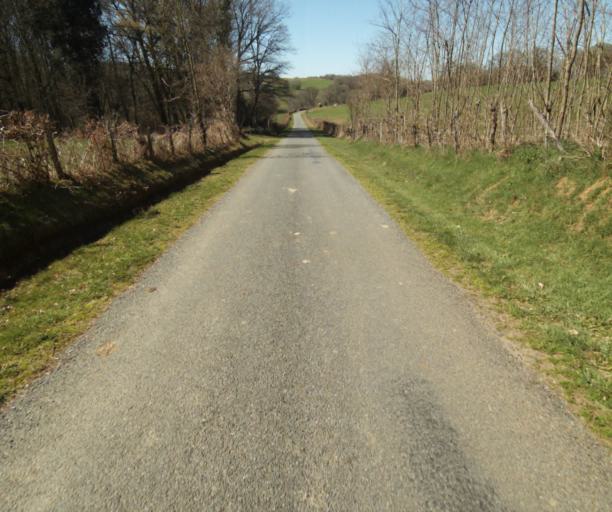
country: FR
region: Limousin
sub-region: Departement de la Correze
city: Uzerche
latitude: 45.3979
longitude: 1.6257
